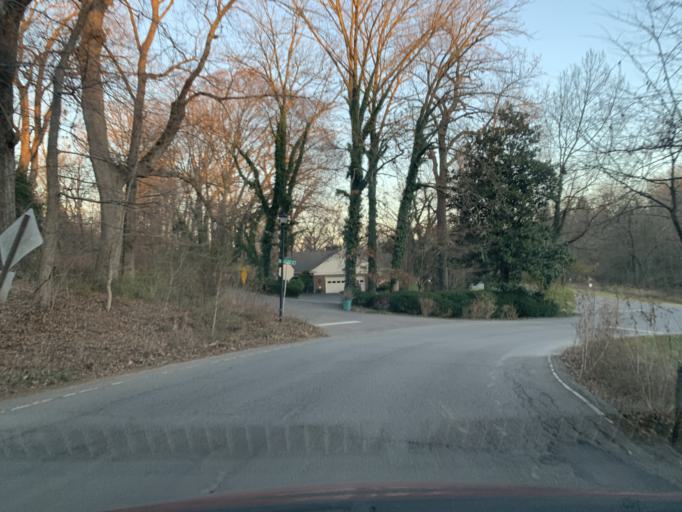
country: US
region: Kentucky
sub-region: Jefferson County
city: Saint Matthews
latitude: 38.2337
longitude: -85.6818
